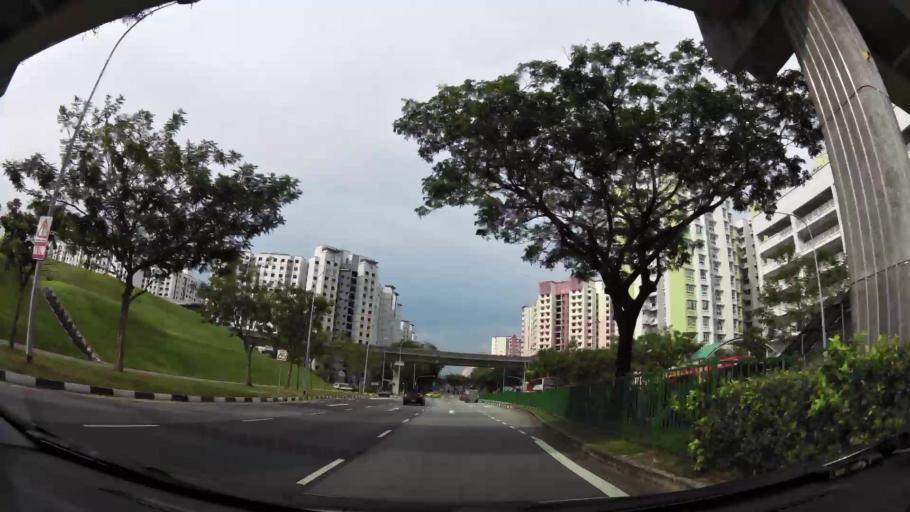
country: MY
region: Johor
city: Kampung Pasir Gudang Baru
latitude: 1.3856
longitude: 103.8910
